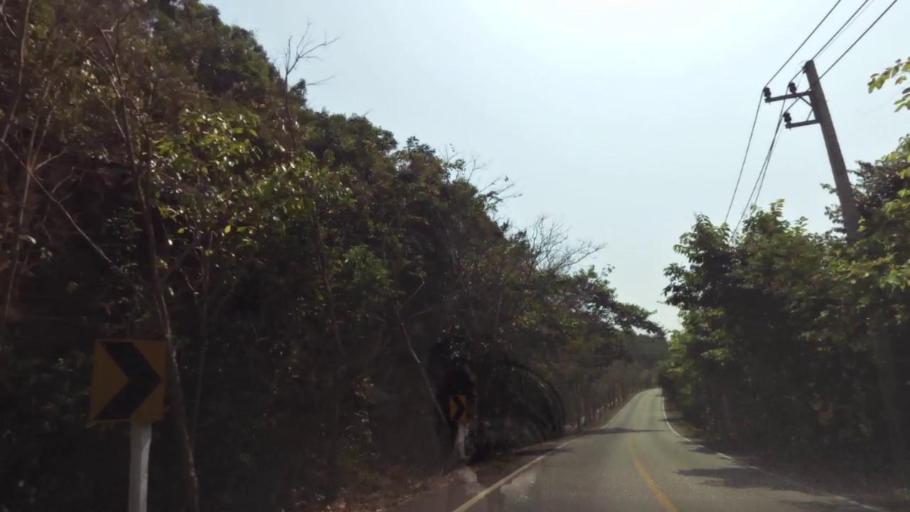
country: TH
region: Chanthaburi
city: Tha Mai
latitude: 12.5273
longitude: 101.9471
